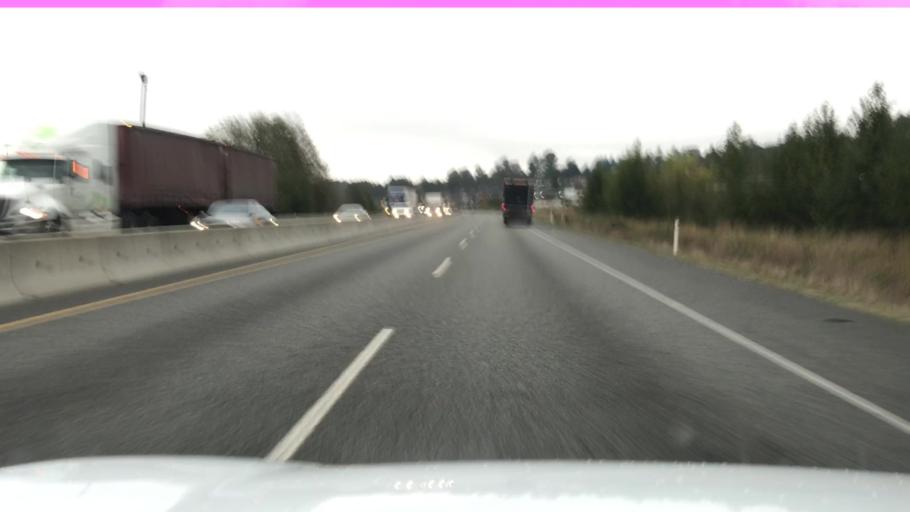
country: CA
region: British Columbia
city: Pitt Meadows
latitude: 49.1963
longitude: -122.7458
